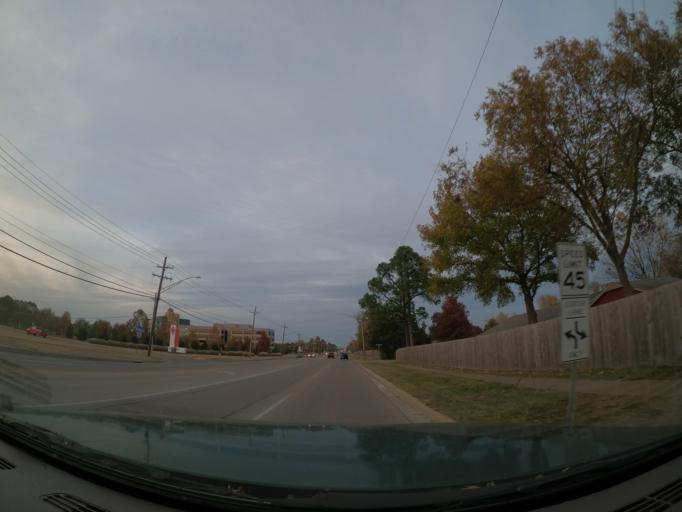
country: US
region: Oklahoma
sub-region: Tulsa County
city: Broken Arrow
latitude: 36.0216
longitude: -95.7974
